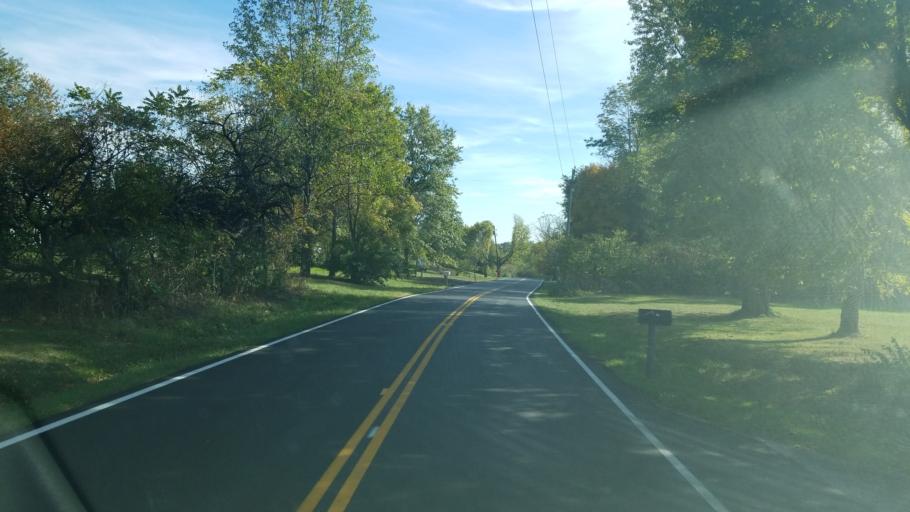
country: US
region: Ohio
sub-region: Warren County
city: Morrow
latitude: 39.4073
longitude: -84.0758
